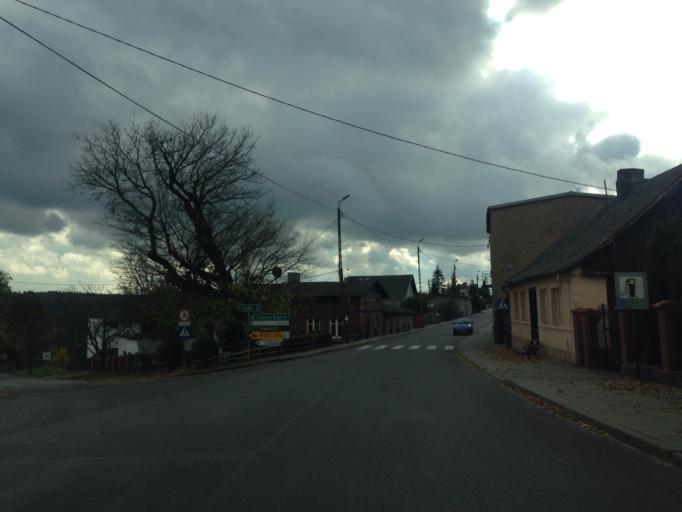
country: PL
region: Kujawsko-Pomorskie
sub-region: Powiat brodnicki
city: Gorzno
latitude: 53.1958
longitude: 19.6457
